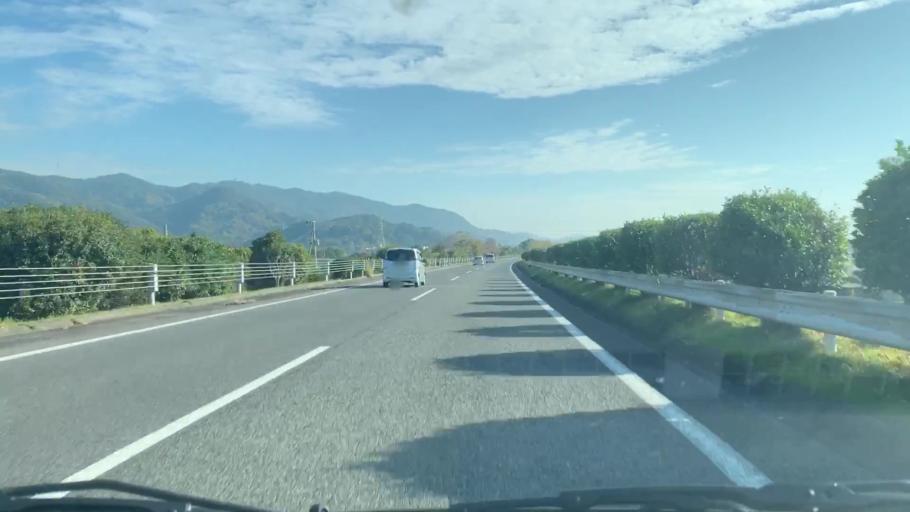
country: JP
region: Saga Prefecture
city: Saga-shi
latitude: 33.3160
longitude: 130.2596
